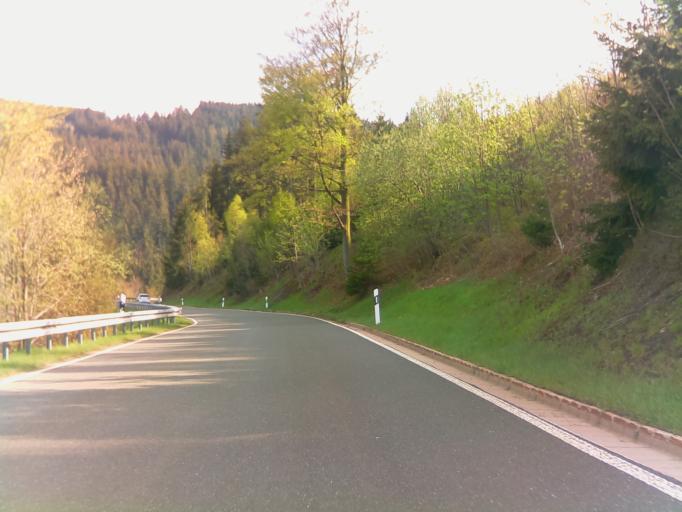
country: DE
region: Thuringia
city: Grafenthal
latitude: 50.5038
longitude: 11.2957
